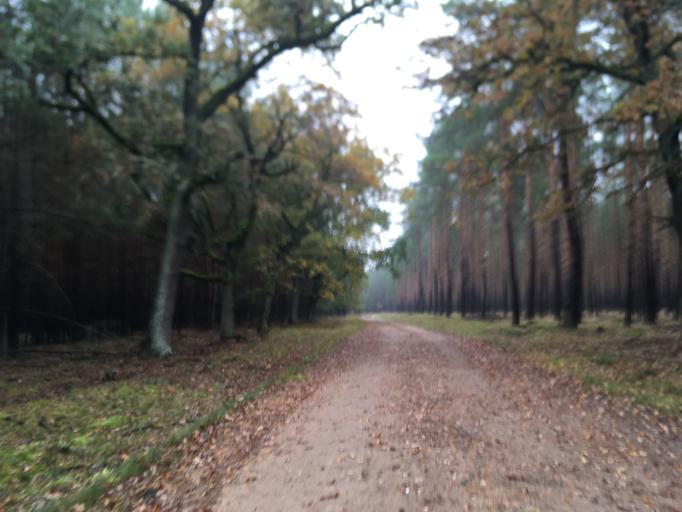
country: DE
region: Brandenburg
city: Beeskow
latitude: 52.2099
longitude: 14.3004
